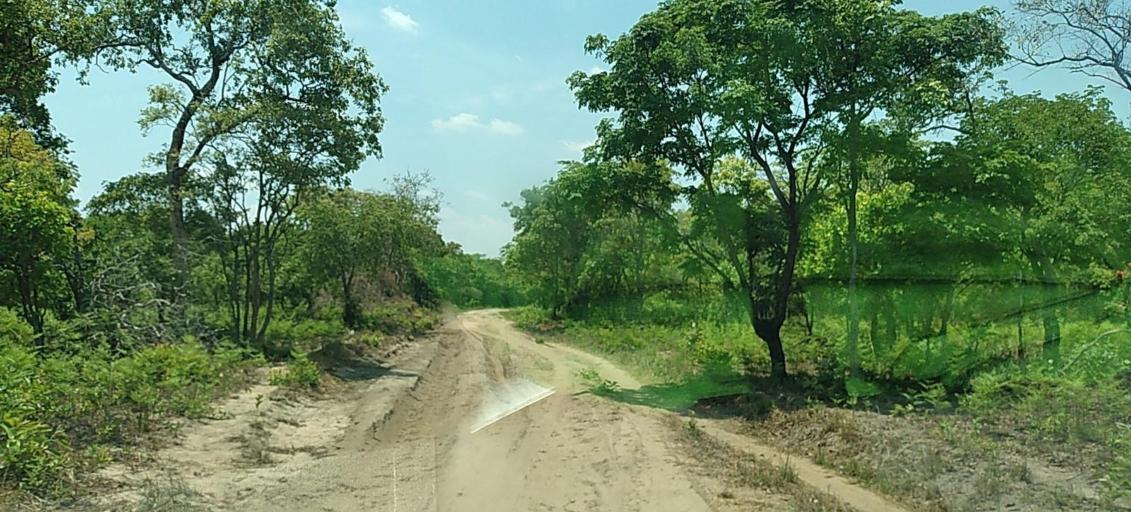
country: CD
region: Katanga
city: Kolwezi
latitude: -11.3437
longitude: 25.2172
